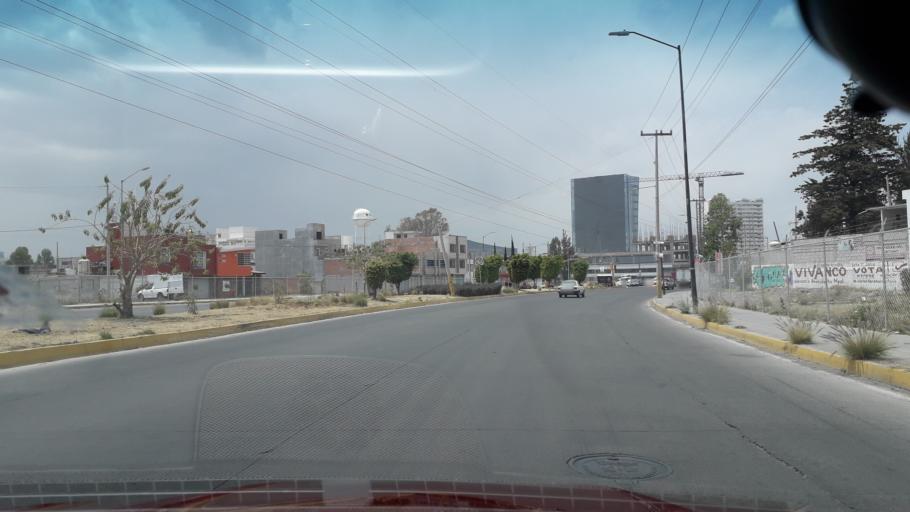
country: MX
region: Puebla
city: Tlazcalancingo
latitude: 19.0066
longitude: -98.2432
